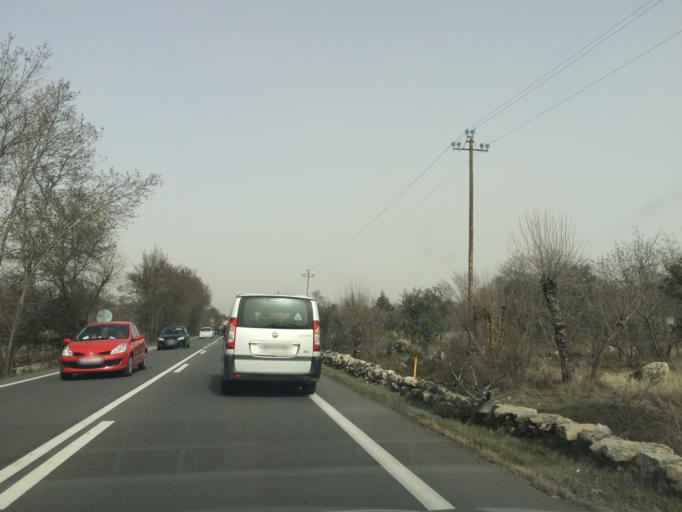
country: ES
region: Madrid
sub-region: Provincia de Madrid
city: Moralzarzal
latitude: 40.6657
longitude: -3.9786
